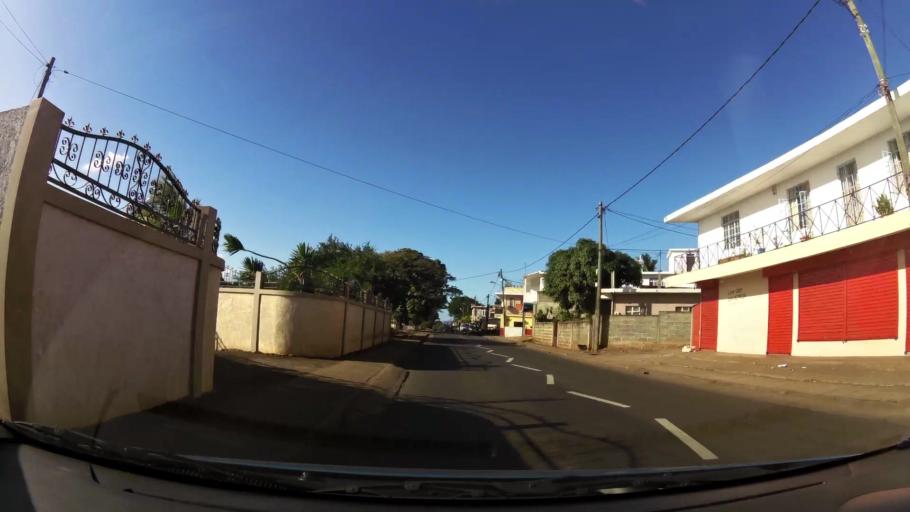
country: MU
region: Black River
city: Petite Riviere
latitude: -20.1907
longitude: 57.4537
